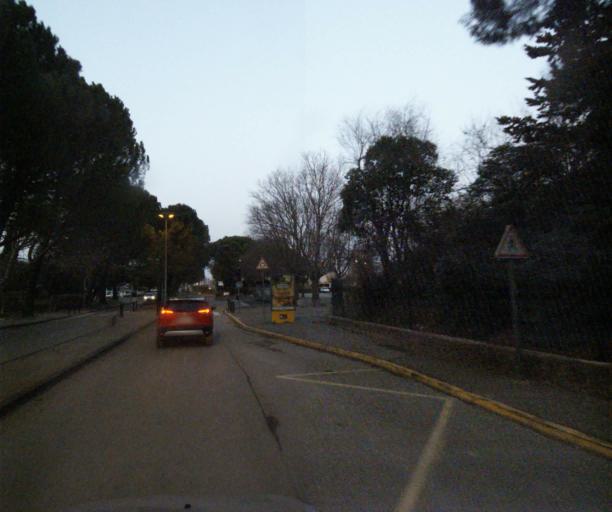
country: FR
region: Provence-Alpes-Cote d'Azur
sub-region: Departement des Bouches-du-Rhone
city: Gardanne
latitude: 43.4558
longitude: 5.4775
